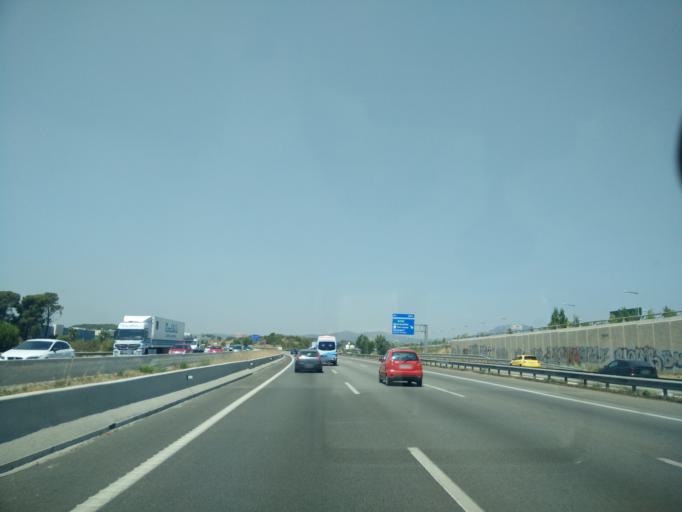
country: ES
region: Catalonia
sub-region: Provincia de Barcelona
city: Sant Quirze del Valles
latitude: 41.5393
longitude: 2.0846
